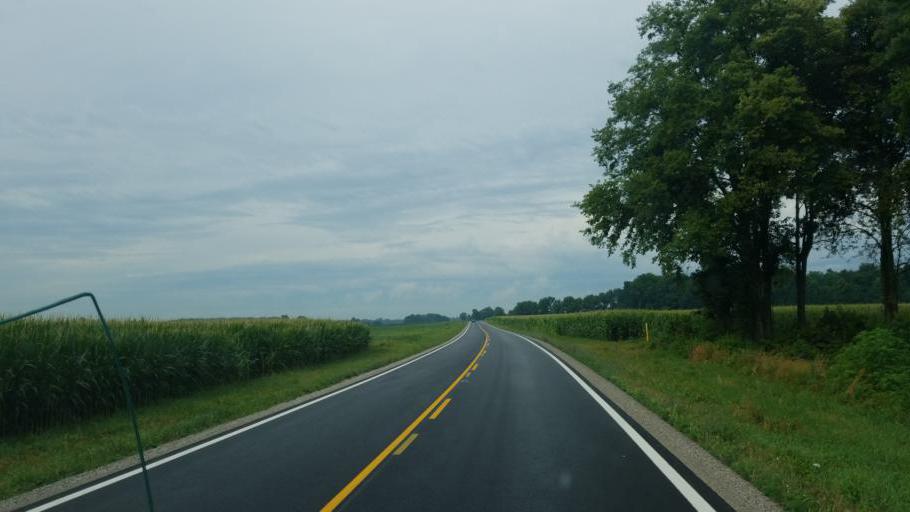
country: US
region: Ohio
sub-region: Defiance County
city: Hicksville
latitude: 41.3487
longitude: -84.6734
